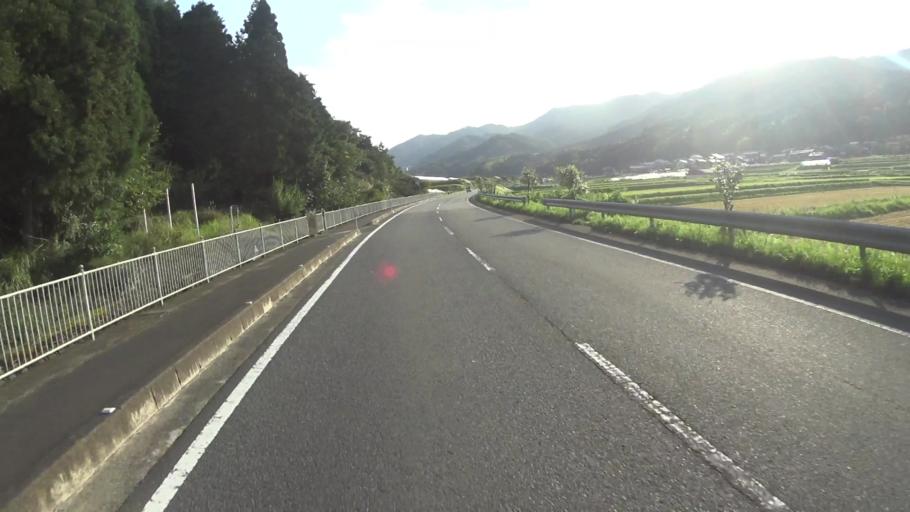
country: JP
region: Kyoto
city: Miyazu
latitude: 35.4735
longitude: 135.0909
